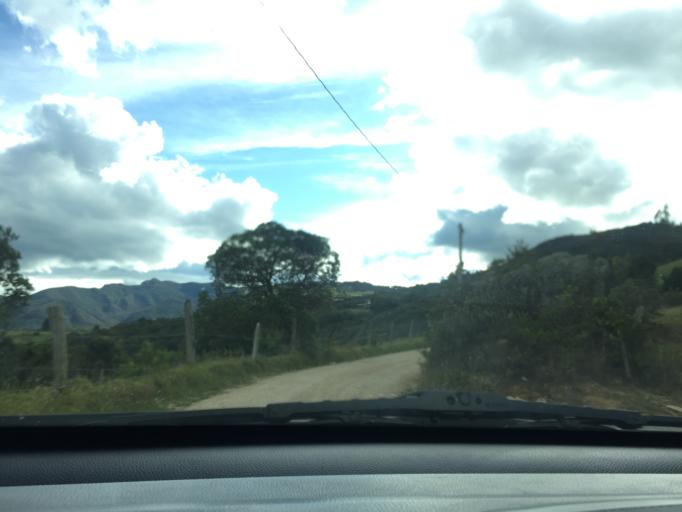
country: CO
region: Cundinamarca
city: Tocancipa
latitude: 4.9283
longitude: -73.8962
